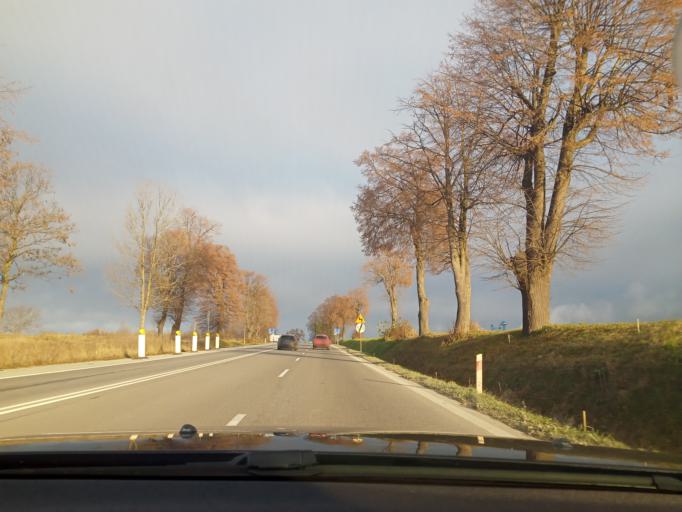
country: PL
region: Lesser Poland Voivodeship
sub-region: Powiat miechowski
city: Miechow
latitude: 50.3198
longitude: 20.0365
